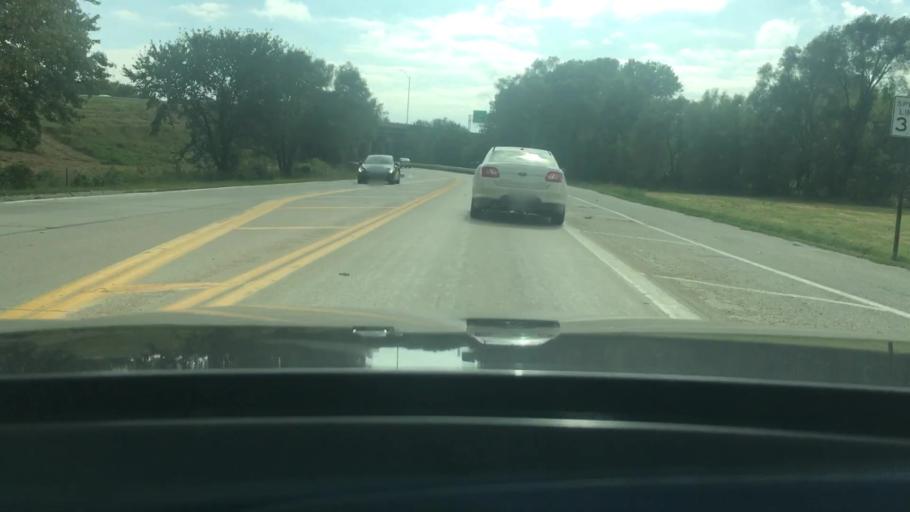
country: US
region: Iowa
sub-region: Pottawattamie County
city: Council Bluffs
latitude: 41.2462
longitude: -95.8173
